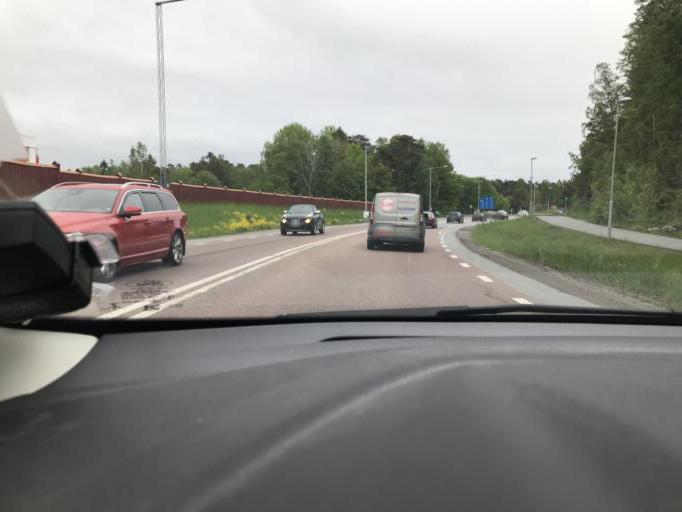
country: SE
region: Stockholm
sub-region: Botkyrka Kommun
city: Alby
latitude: 59.2344
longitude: 17.8417
